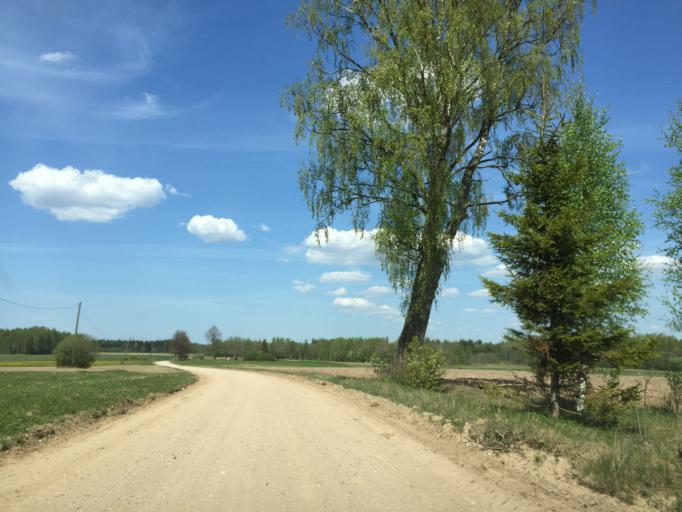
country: LV
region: Limbazu Rajons
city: Limbazi
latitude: 57.3543
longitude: 24.6469
